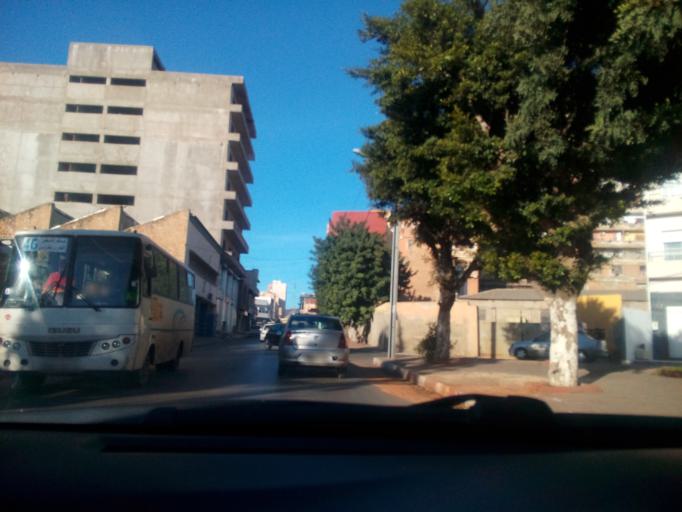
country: DZ
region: Oran
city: Oran
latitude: 35.6868
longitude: -0.6549
